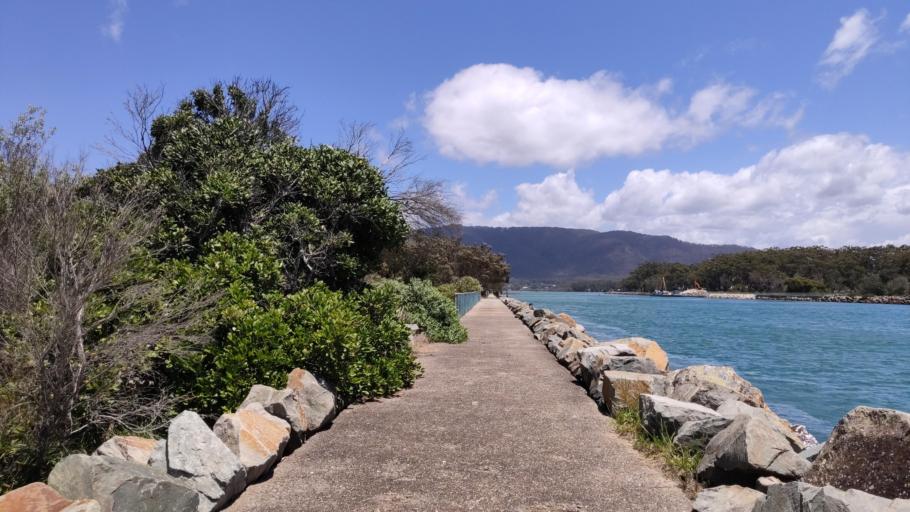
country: AU
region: New South Wales
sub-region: Port Macquarie-Hastings
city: North Haven
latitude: -31.6385
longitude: 152.8305
